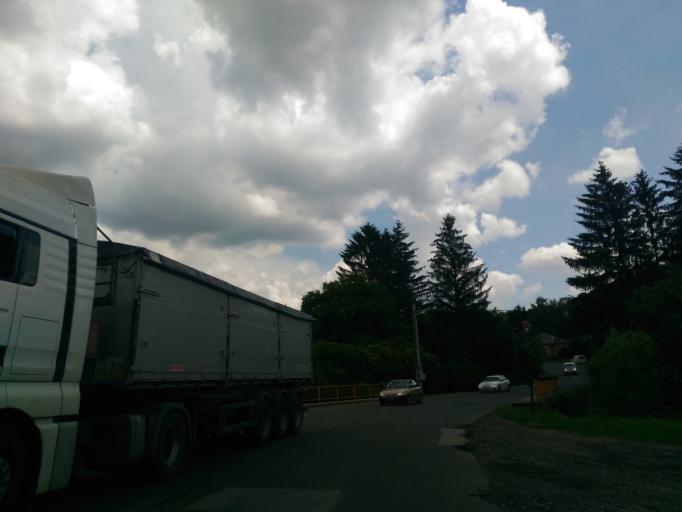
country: HU
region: Baranya
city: Komlo
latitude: 46.1607
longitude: 18.2339
